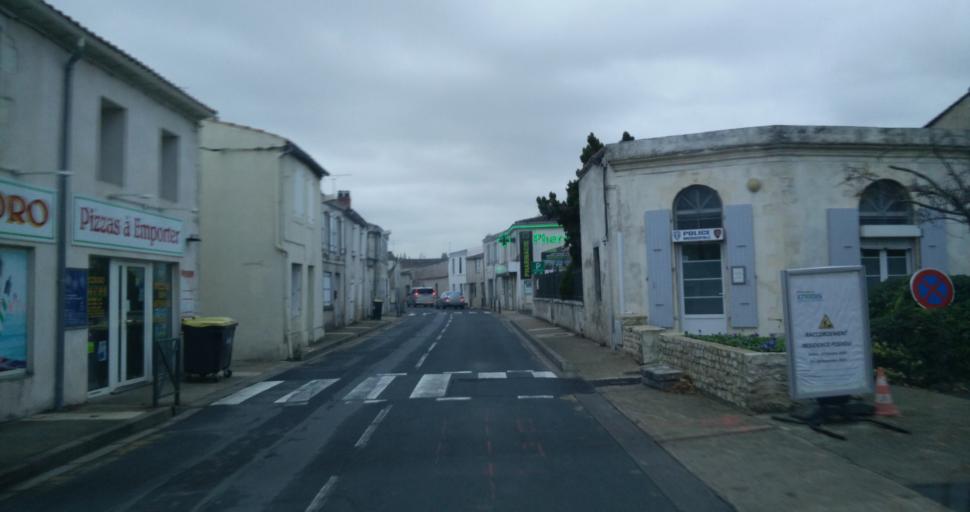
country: FR
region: Poitou-Charentes
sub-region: Departement de la Charente-Maritime
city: Puilboreau
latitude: 46.1875
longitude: -1.1184
